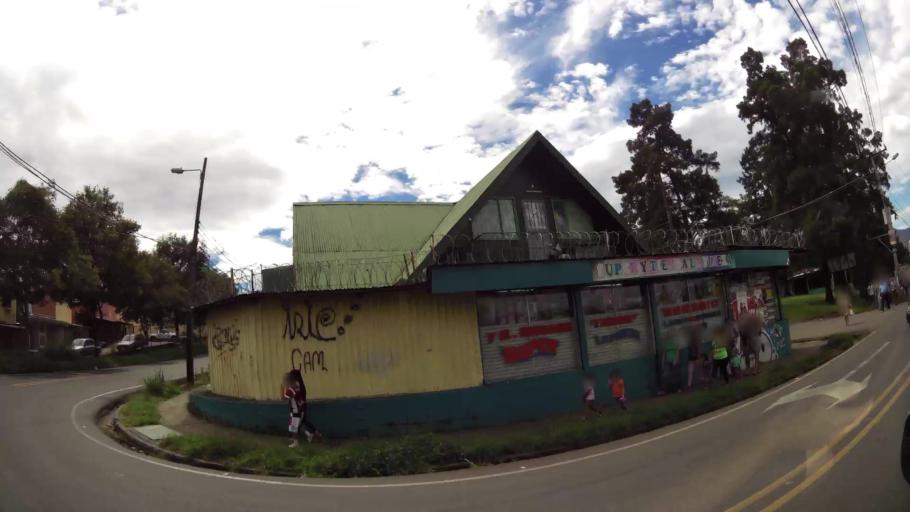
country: CR
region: San Jose
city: Alajuelita
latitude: 9.9040
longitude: -84.0758
